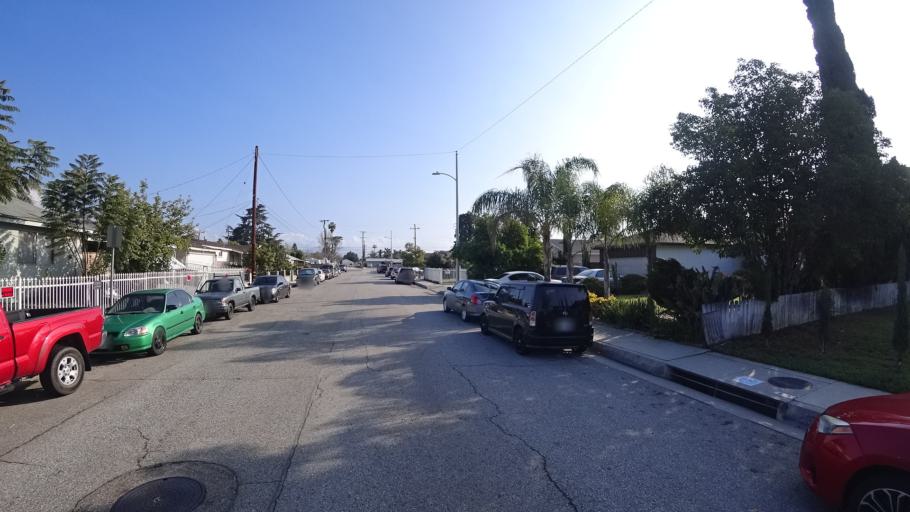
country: US
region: California
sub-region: Los Angeles County
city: Baldwin Park
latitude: 34.0767
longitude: -117.9510
